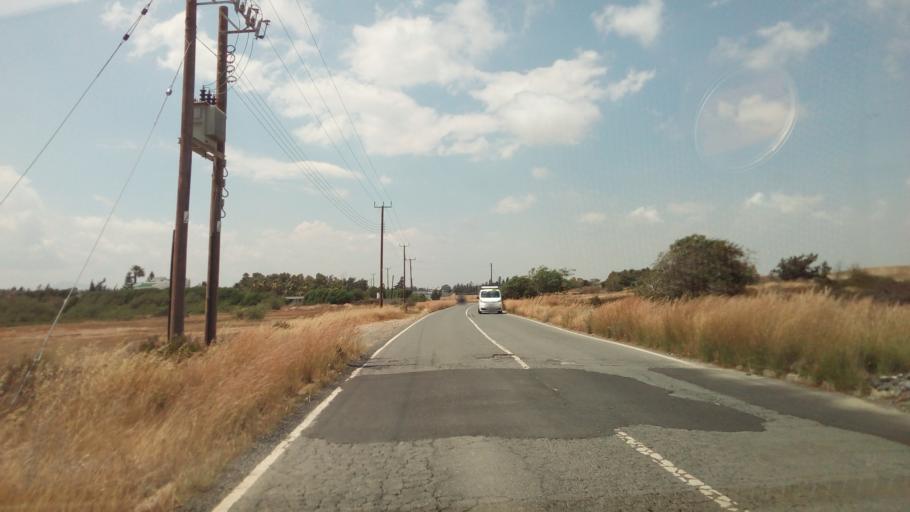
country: CY
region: Larnaka
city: Meneou
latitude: 34.8508
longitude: 33.6105
